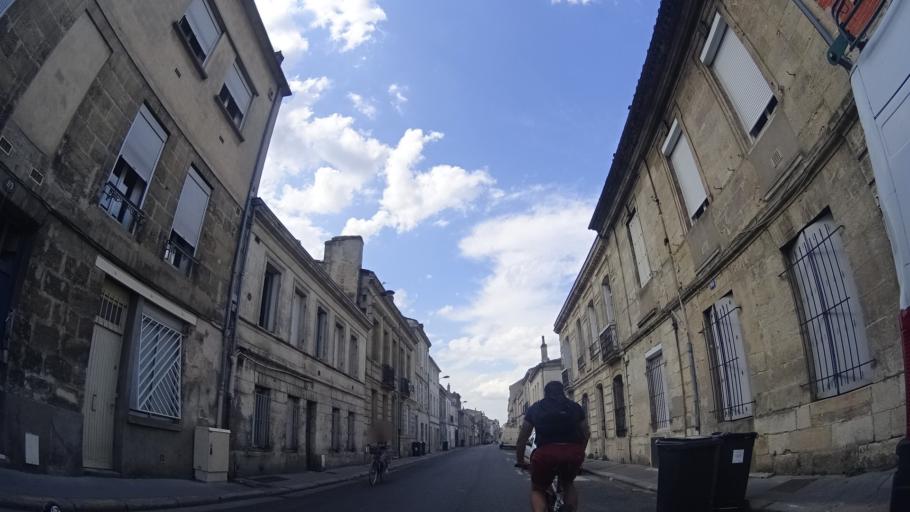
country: FR
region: Aquitaine
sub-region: Departement de la Gironde
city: Bordeaux
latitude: 44.8256
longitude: -0.5672
